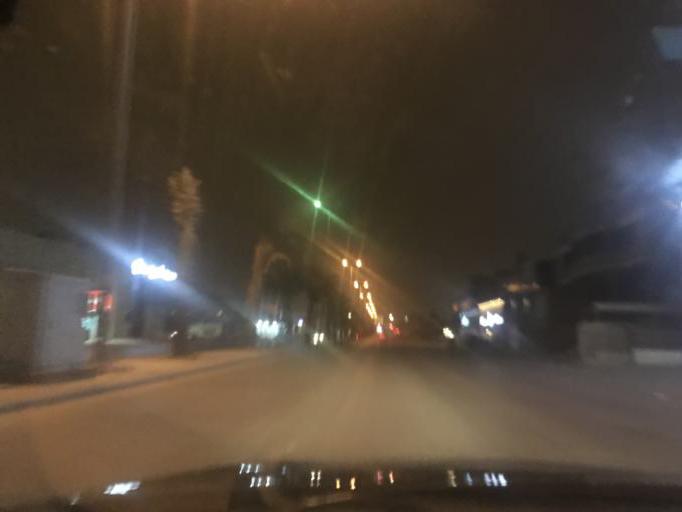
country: SA
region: Ar Riyad
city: Riyadh
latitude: 24.7498
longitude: 46.7789
